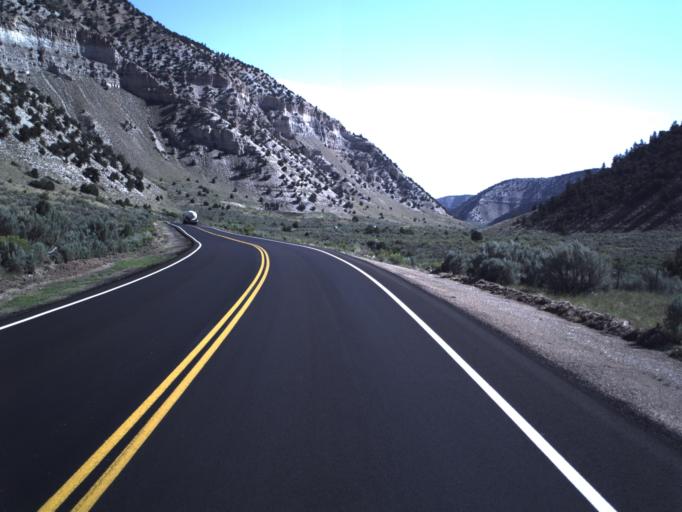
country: US
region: Utah
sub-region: Duchesne County
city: Duchesne
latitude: 39.9971
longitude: -110.5859
